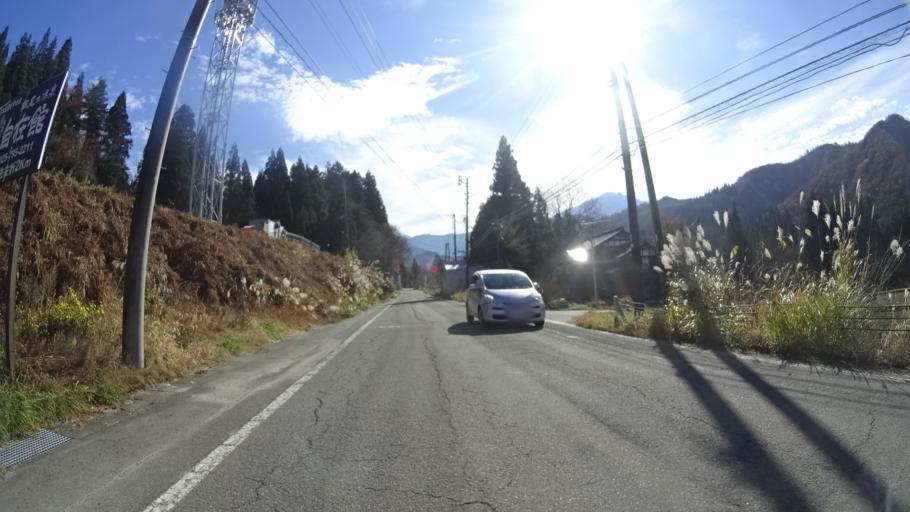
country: JP
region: Niigata
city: Muikamachi
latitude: 37.2012
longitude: 139.0756
